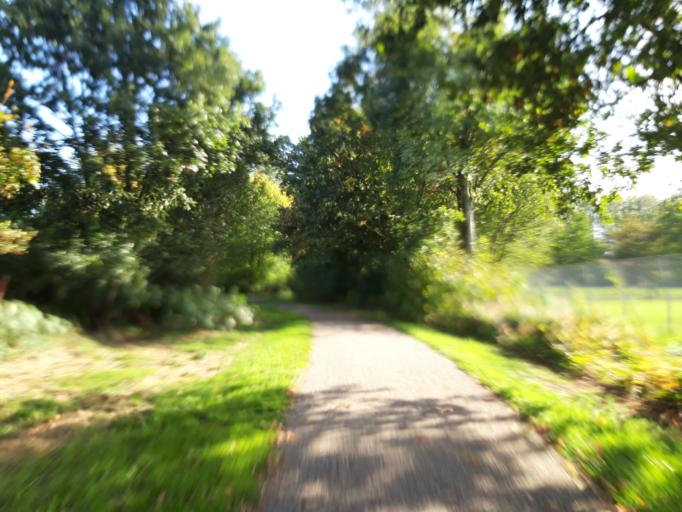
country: NL
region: Utrecht
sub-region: Gemeente Woerden
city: Woerden
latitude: 52.0726
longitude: 4.8731
